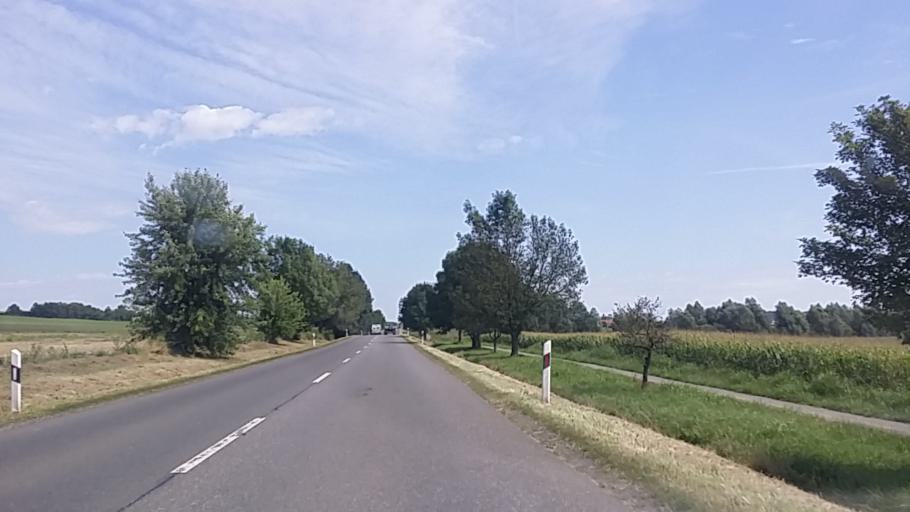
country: HU
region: Baranya
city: Sasd
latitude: 46.2971
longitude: 18.1238
